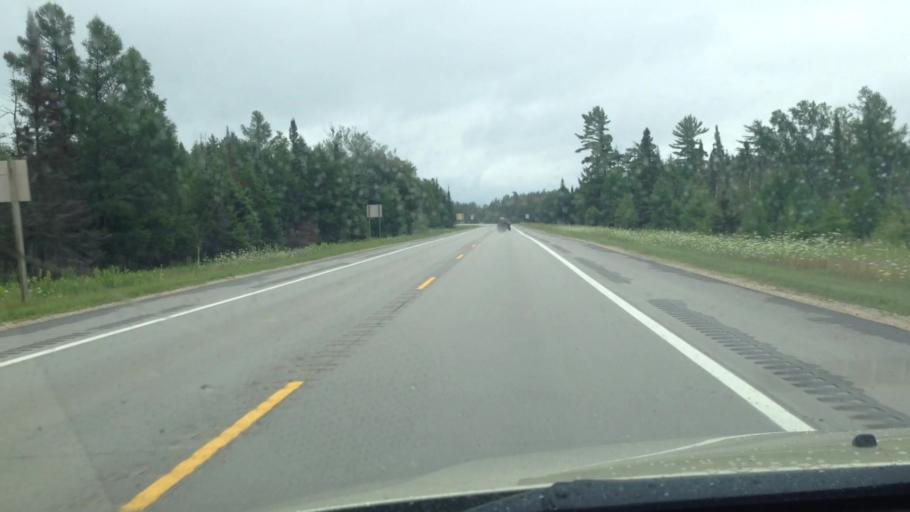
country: US
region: Michigan
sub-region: Schoolcraft County
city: Manistique
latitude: 45.8901
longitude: -86.5312
